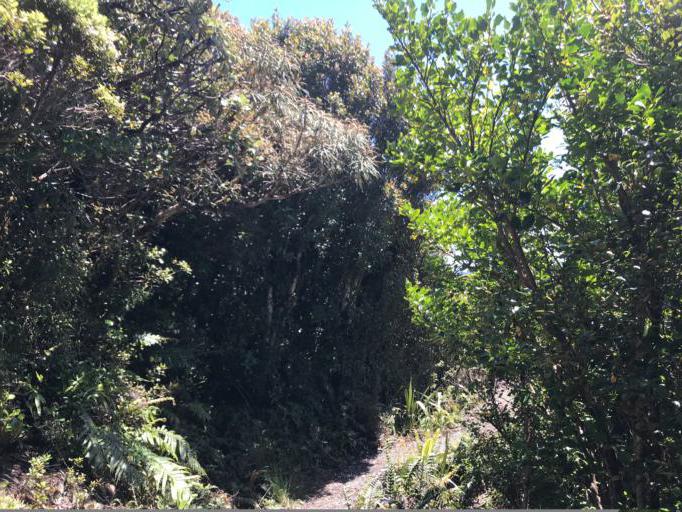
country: NZ
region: Wellington
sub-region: Kapiti Coast District
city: Otaki
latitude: -40.9089
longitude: 175.2580
